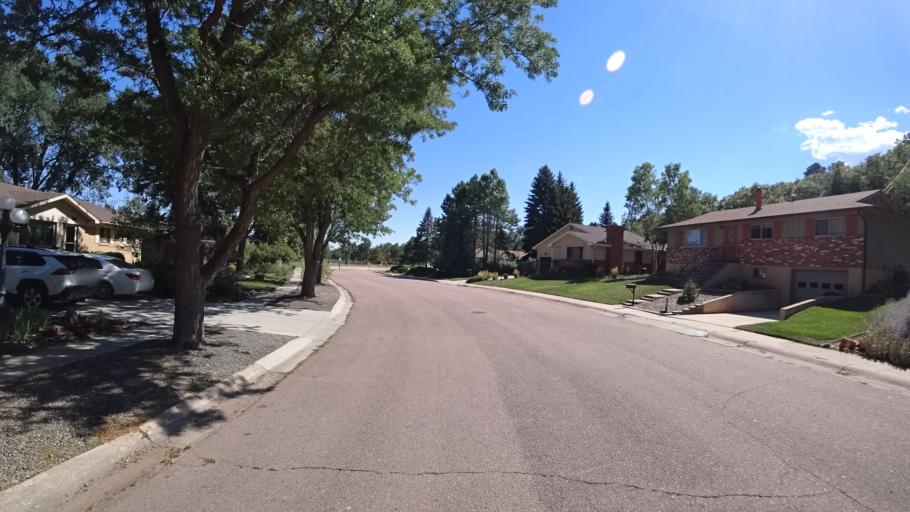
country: US
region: Colorado
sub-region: El Paso County
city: Manitou Springs
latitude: 38.8653
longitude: -104.8725
